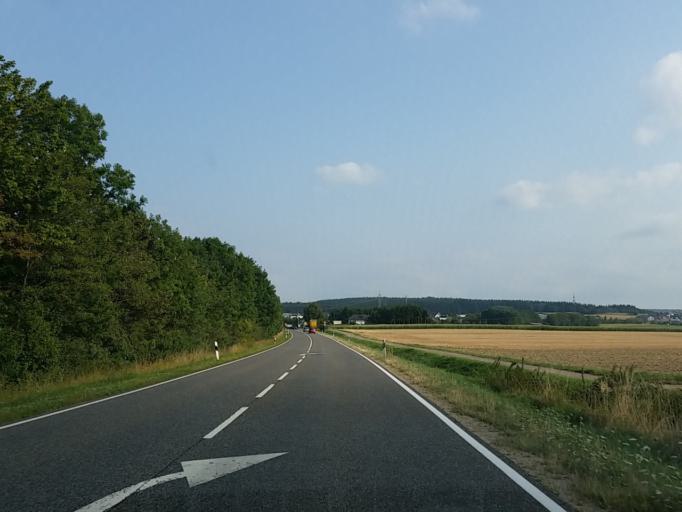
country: DE
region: Rheinland-Pfalz
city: Thomm
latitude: 49.7309
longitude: 6.8010
